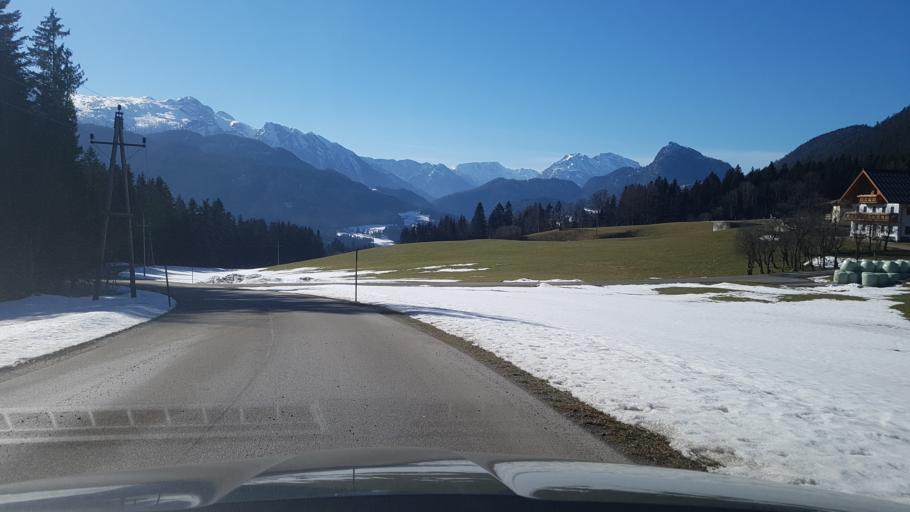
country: AT
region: Salzburg
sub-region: Politischer Bezirk Hallein
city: Abtenau
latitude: 47.6024
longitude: 13.3553
